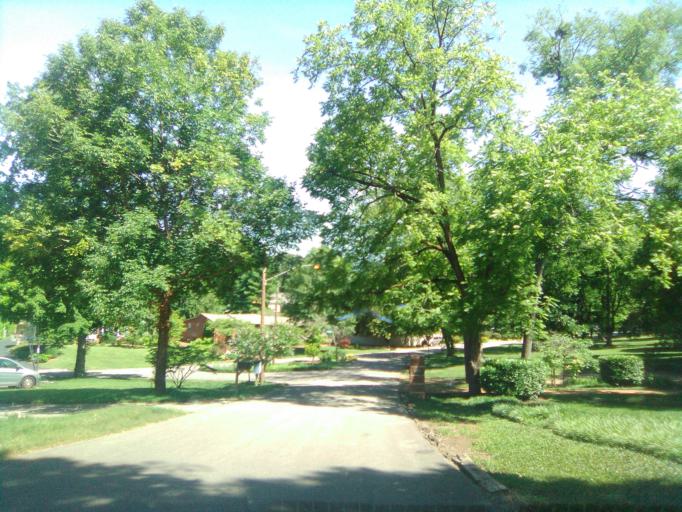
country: US
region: Tennessee
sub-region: Davidson County
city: Belle Meade
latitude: 36.1232
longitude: -86.8365
